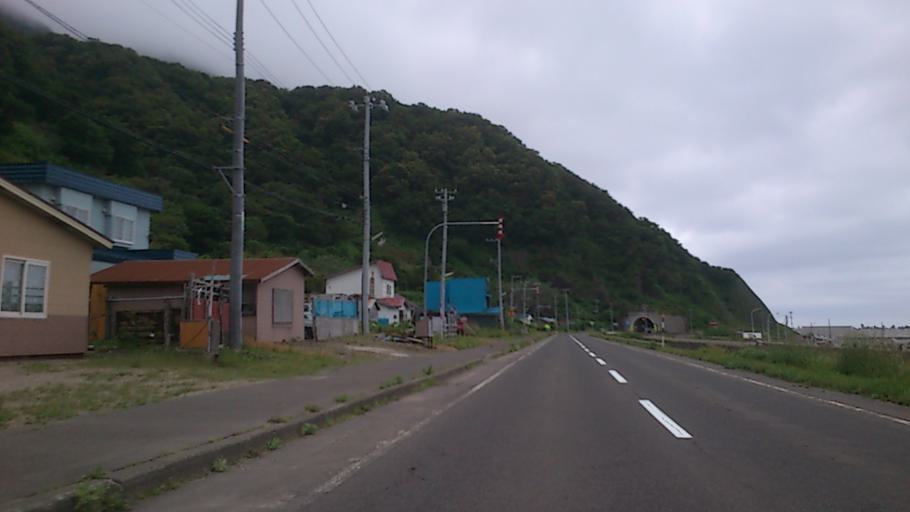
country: JP
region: Hokkaido
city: Iwanai
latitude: 42.6718
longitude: 139.8859
